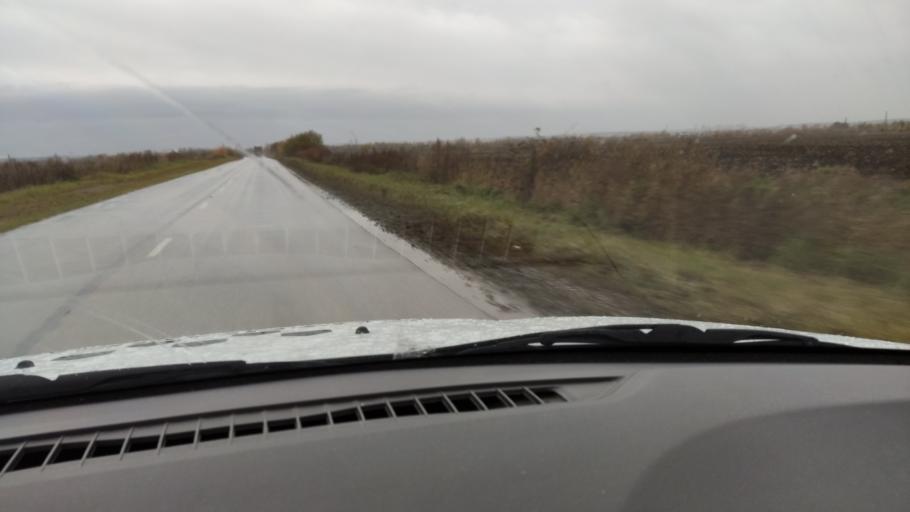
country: RU
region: Perm
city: Kondratovo
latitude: 57.9924
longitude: 56.0914
